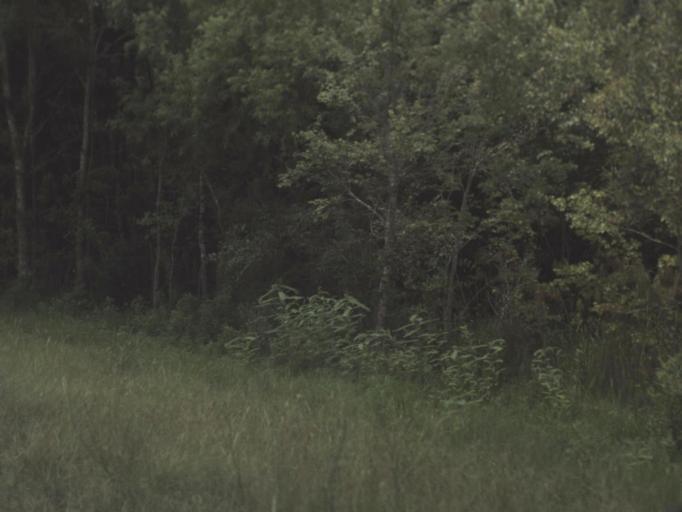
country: US
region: Florida
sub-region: Union County
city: Lake Butler
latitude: 29.9192
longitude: -82.4050
